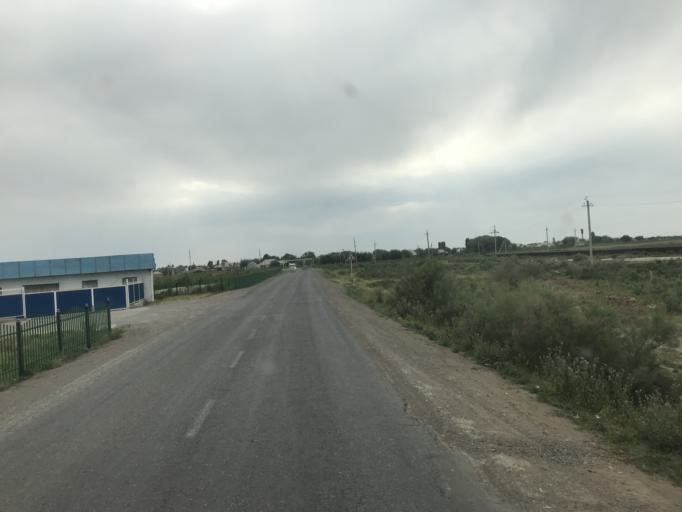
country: KZ
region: Ongtustik Qazaqstan
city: Asykata
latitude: 40.9075
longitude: 68.3709
